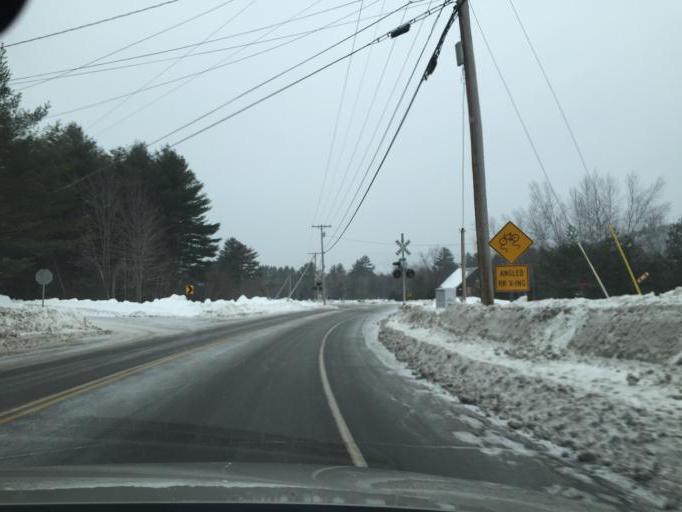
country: US
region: New Hampshire
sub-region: Carroll County
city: North Conway
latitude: 44.0816
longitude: -71.2425
